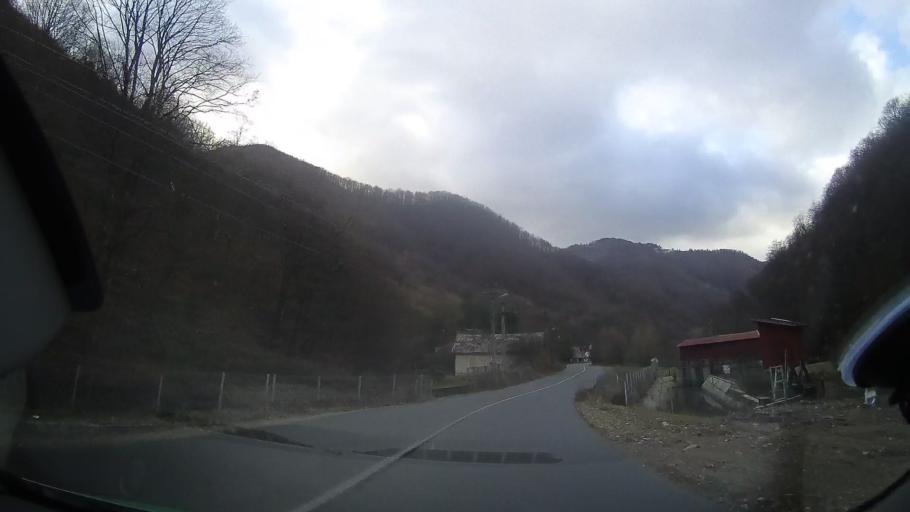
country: RO
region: Cluj
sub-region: Comuna Maguri-Racatau
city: Maguri-Racatau
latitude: 46.6712
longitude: 23.2521
